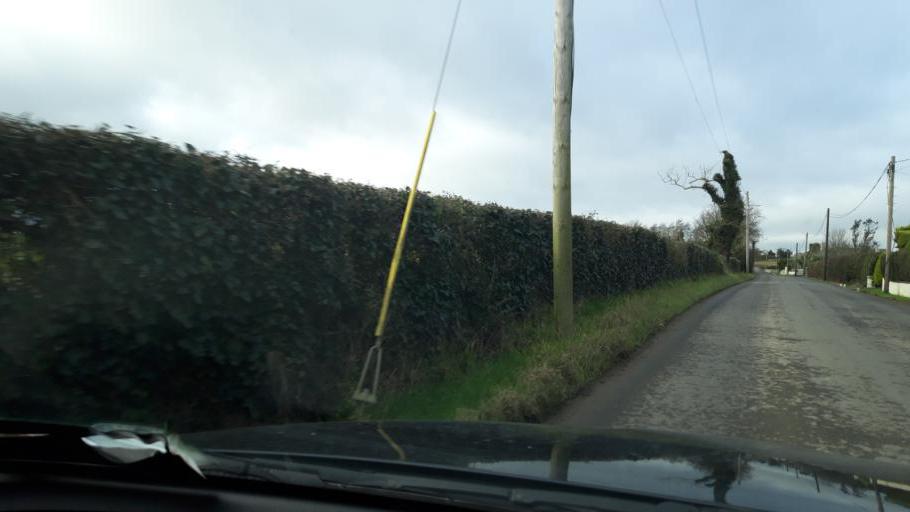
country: IE
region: Leinster
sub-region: Fingal County
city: Skerries
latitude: 53.5580
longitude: -6.1370
